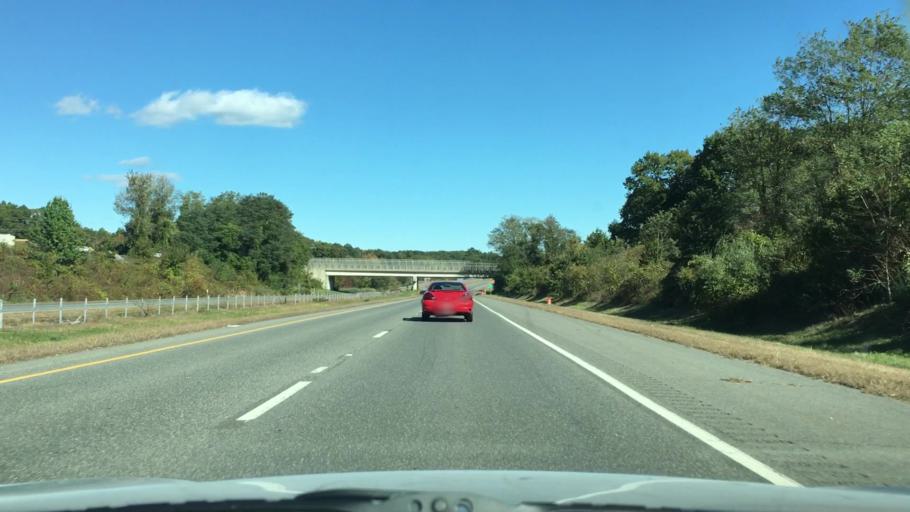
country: US
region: Massachusetts
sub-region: Hampden County
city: Agawam
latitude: 42.0612
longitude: -72.6595
